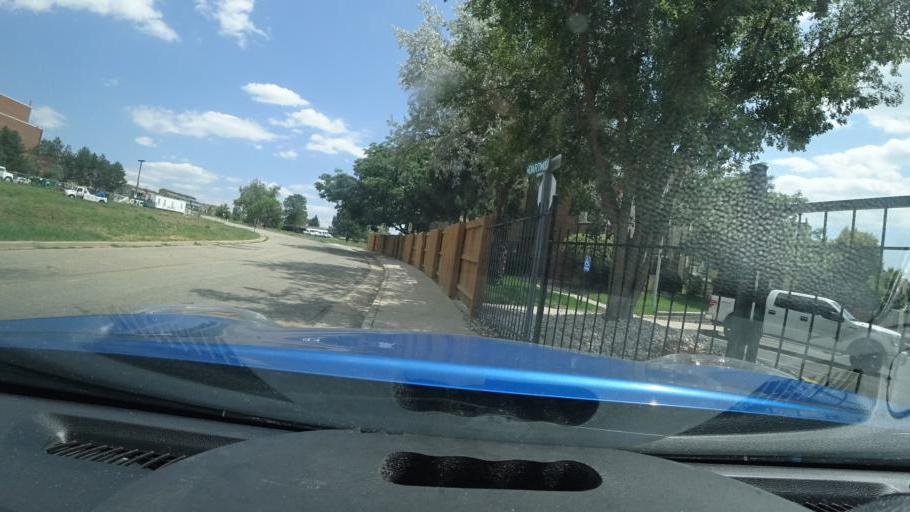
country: US
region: Colorado
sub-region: Arapahoe County
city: Sheridan
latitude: 39.6594
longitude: -105.0302
